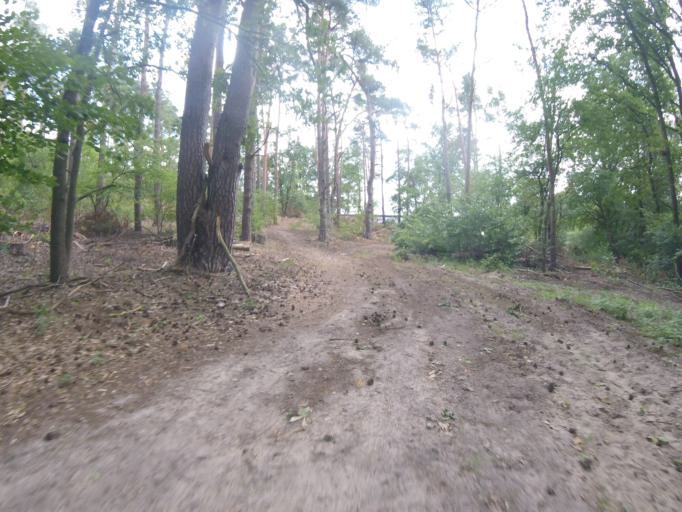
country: DE
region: Brandenburg
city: Bestensee
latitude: 52.2450
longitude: 13.6151
